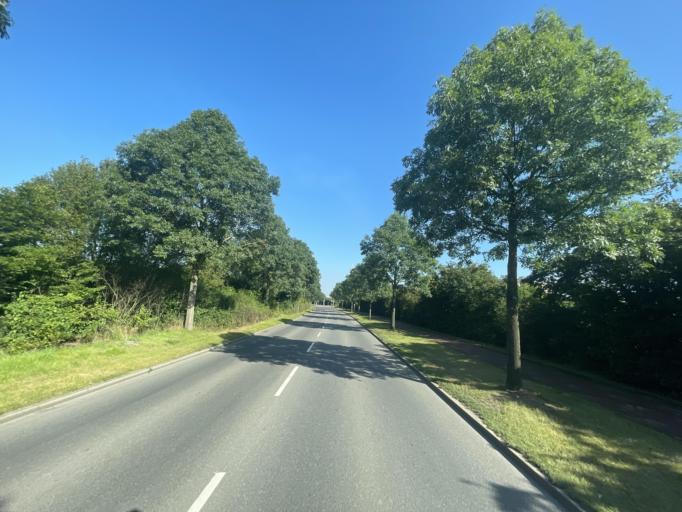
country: DE
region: North Rhine-Westphalia
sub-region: Regierungsbezirk Dusseldorf
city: Meerbusch
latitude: 51.3295
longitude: 6.6773
